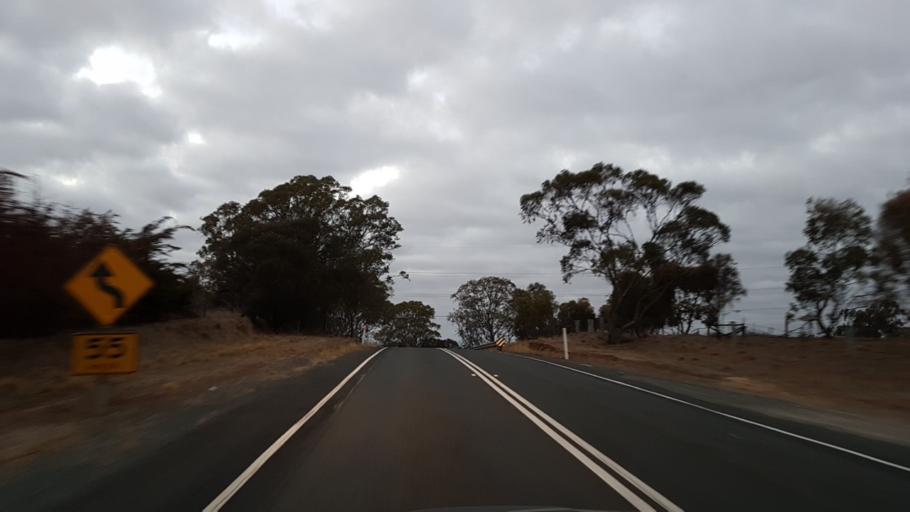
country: AU
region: South Australia
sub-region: Mount Barker
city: Callington
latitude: -35.0468
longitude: 138.9978
